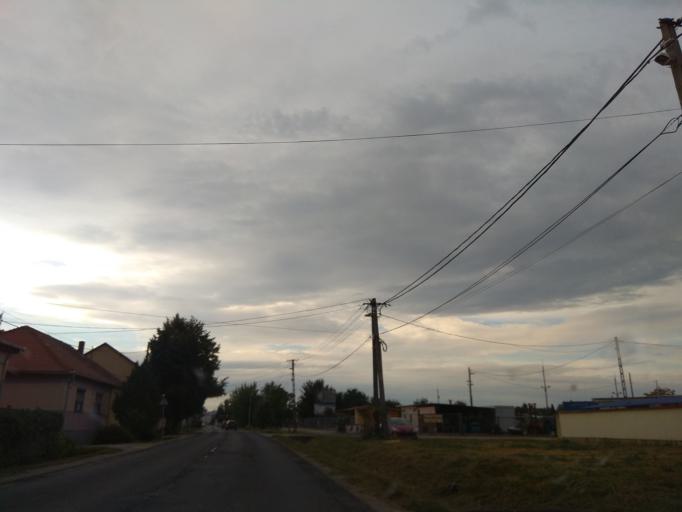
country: HU
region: Borsod-Abauj-Zemplen
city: Miskolc
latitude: 48.0858
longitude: 20.8170
